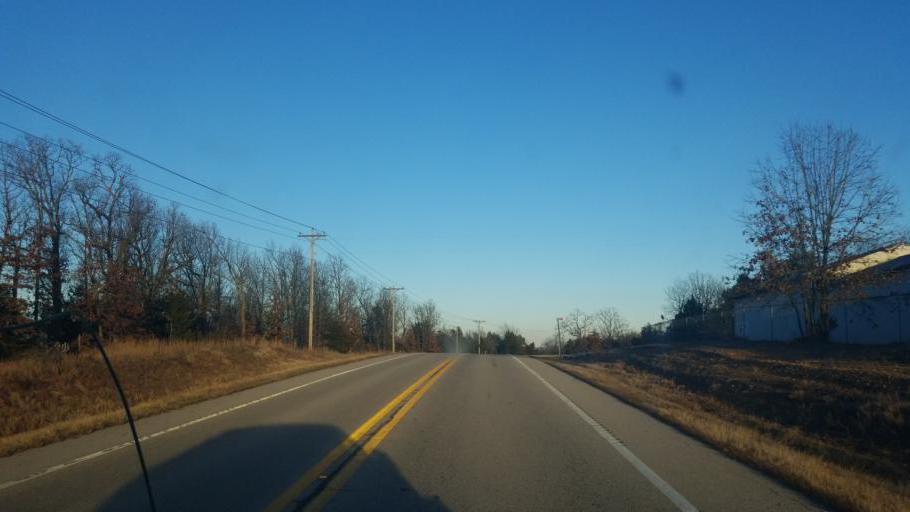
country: US
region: Arkansas
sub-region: Baxter County
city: Mountain Home
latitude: 36.3856
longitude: -92.1816
